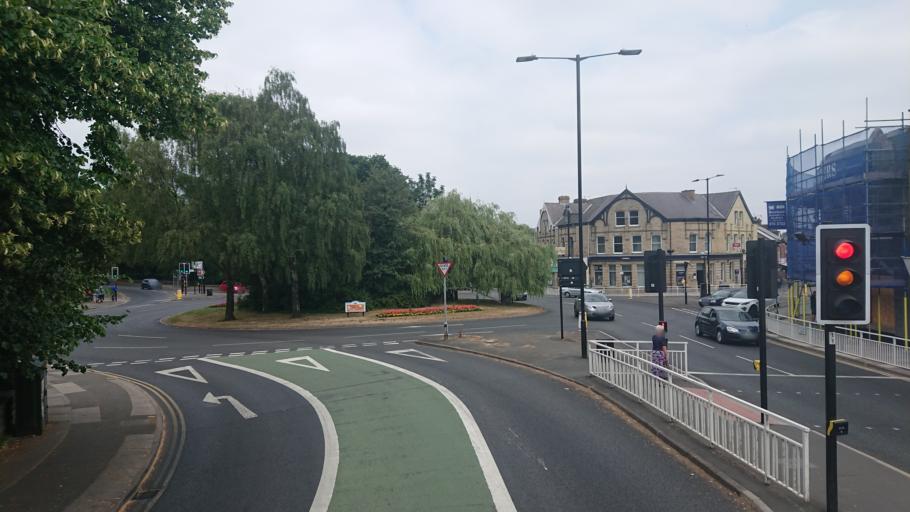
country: GB
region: England
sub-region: Sheffield
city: Sheffield
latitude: 53.3673
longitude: -1.5028
